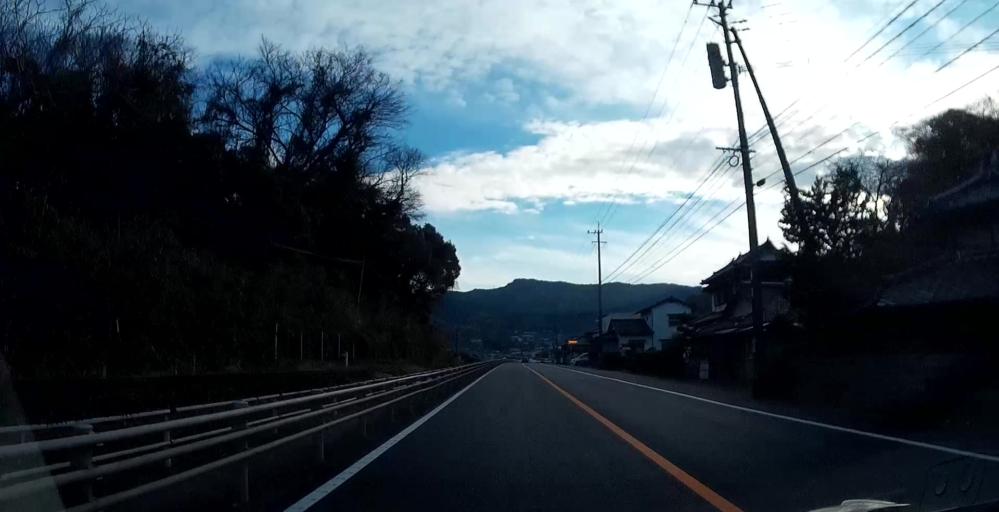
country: JP
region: Kumamoto
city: Uto
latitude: 32.6741
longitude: 130.5526
